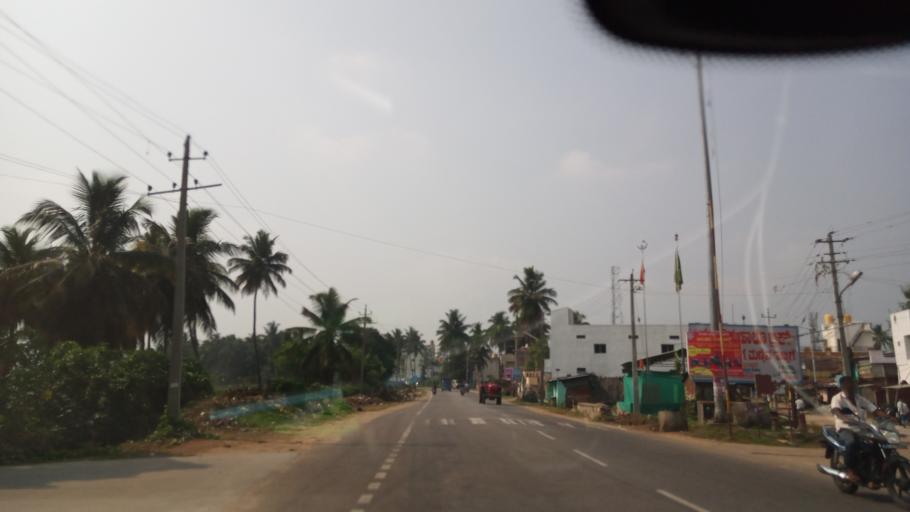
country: IN
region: Karnataka
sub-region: Mandya
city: Pandavapura
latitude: 12.5065
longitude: 76.6750
